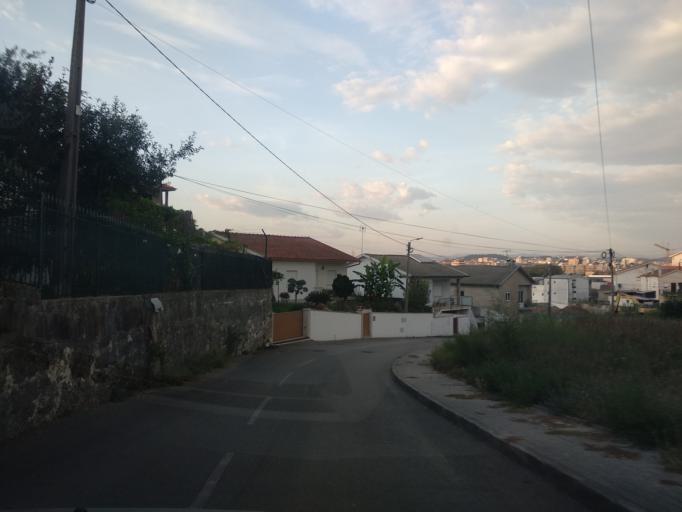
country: PT
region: Braga
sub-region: Braga
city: Braga
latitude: 41.5290
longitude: -8.4503
